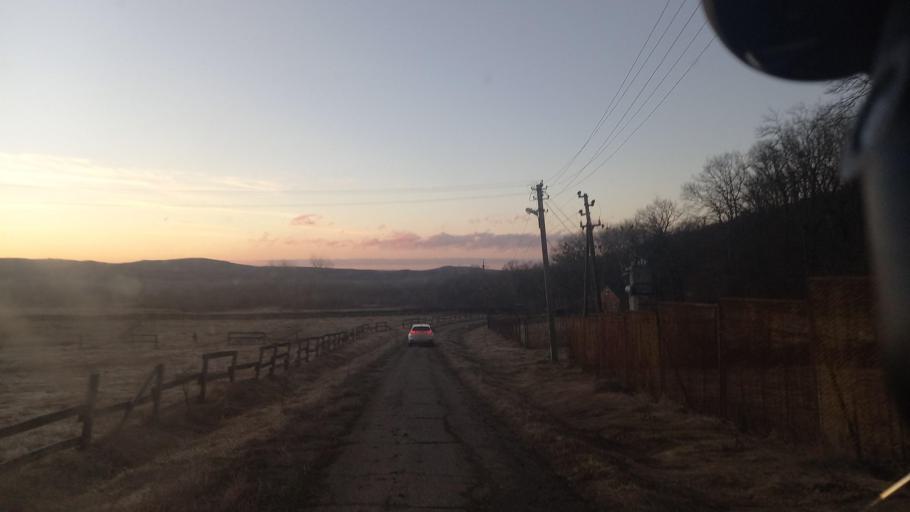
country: RU
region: Krasnodarskiy
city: Smolenskaya
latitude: 44.7245
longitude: 38.8436
